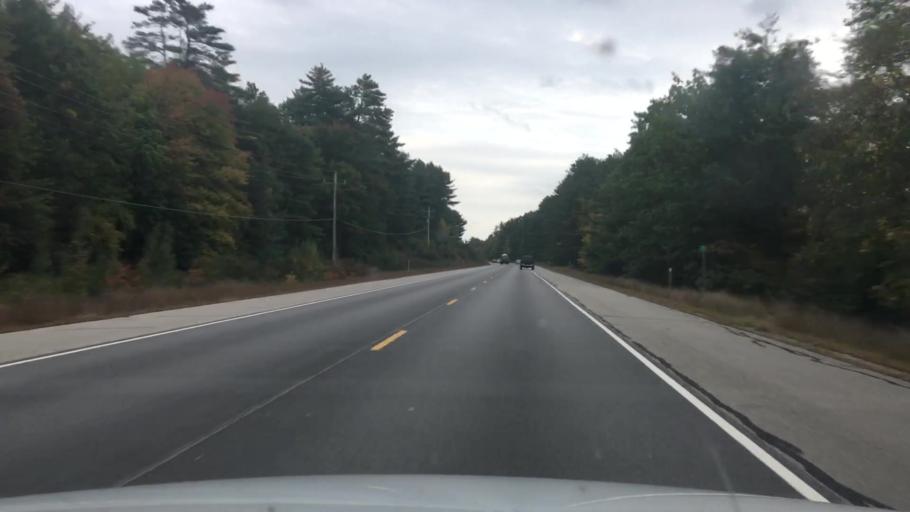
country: US
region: New Hampshire
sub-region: Strafford County
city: New Durham
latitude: 43.4442
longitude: -71.1993
